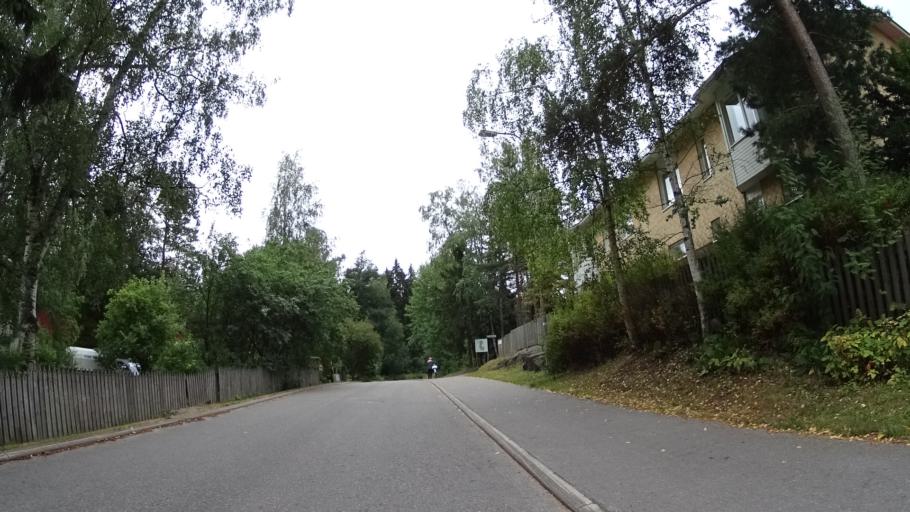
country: FI
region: Uusimaa
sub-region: Helsinki
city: Kilo
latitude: 60.1964
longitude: 24.7592
